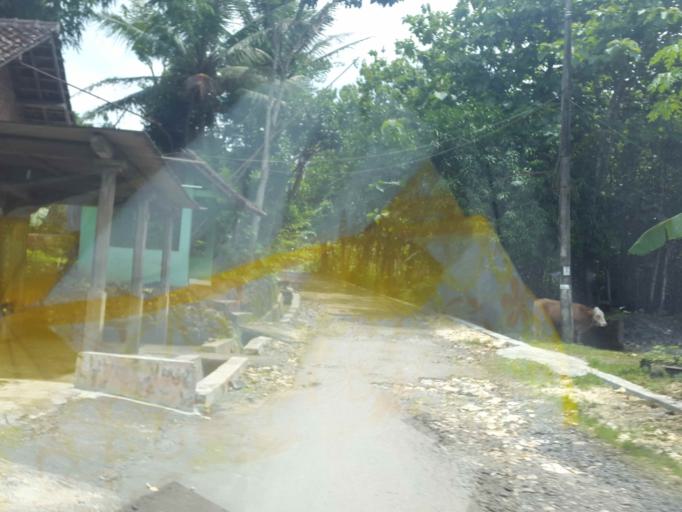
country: ID
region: Daerah Istimewa Yogyakarta
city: Wonosari
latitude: -7.9281
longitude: 110.6123
